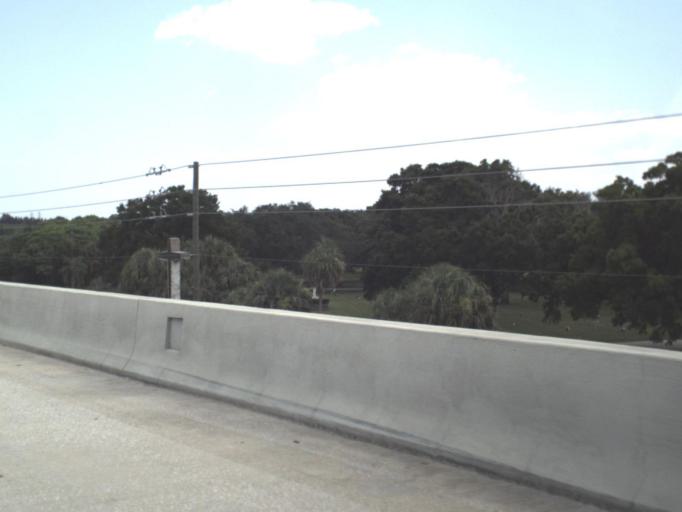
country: US
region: Florida
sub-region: Pinellas County
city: South Highpoint
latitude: 27.8794
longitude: -82.7121
